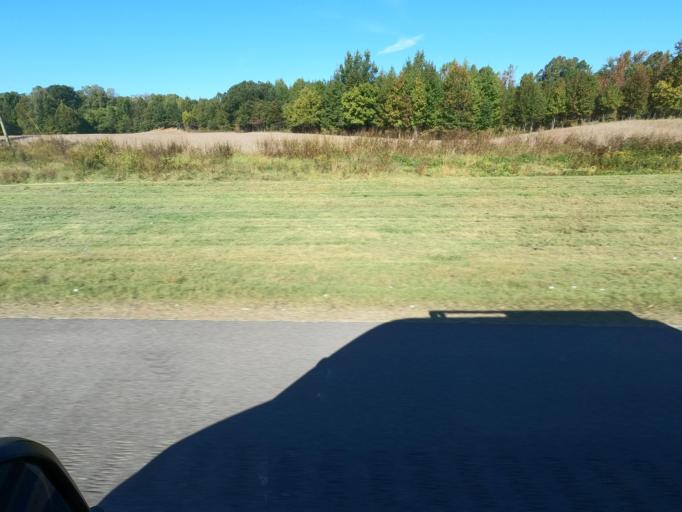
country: US
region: Tennessee
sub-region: Tipton County
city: Atoka
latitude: 35.4593
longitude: -89.7700
